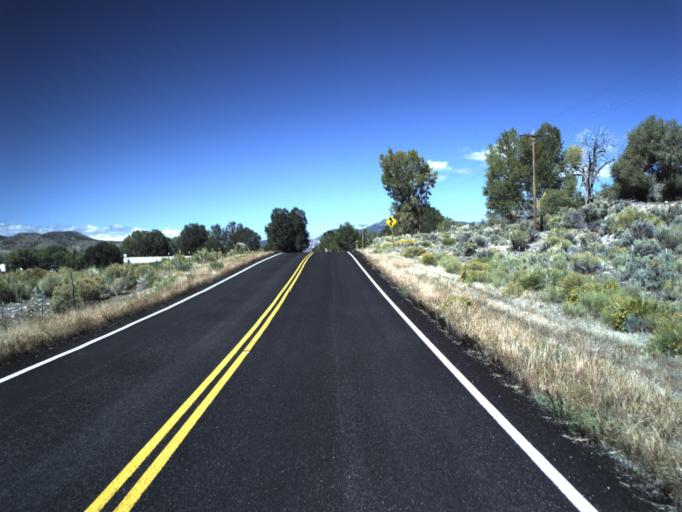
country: US
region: Utah
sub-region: Piute County
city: Junction
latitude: 38.1095
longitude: -111.9882
